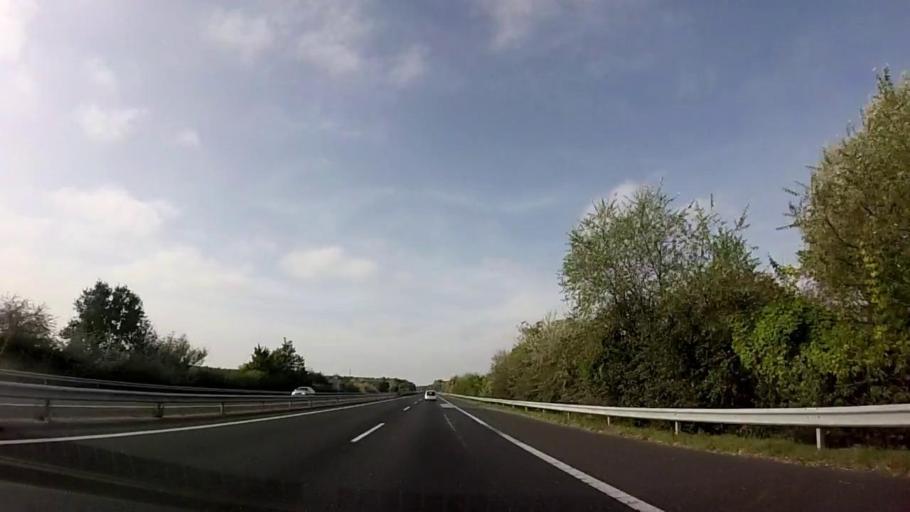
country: HU
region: Fejer
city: Polgardi
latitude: 47.0385
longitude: 18.2872
